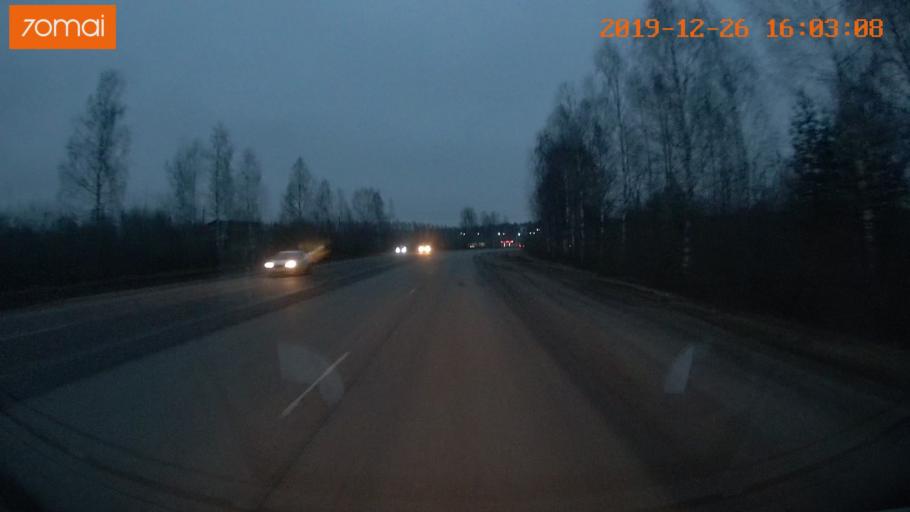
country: RU
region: Jaroslavl
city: Rybinsk
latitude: 58.0114
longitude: 38.8507
